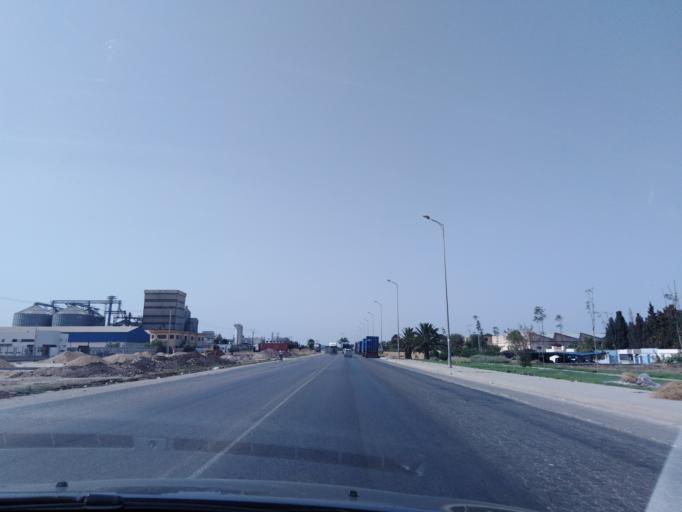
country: MA
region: Chaouia-Ouardigha
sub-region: Settat Province
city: Berrechid
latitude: 33.2420
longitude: -7.5870
